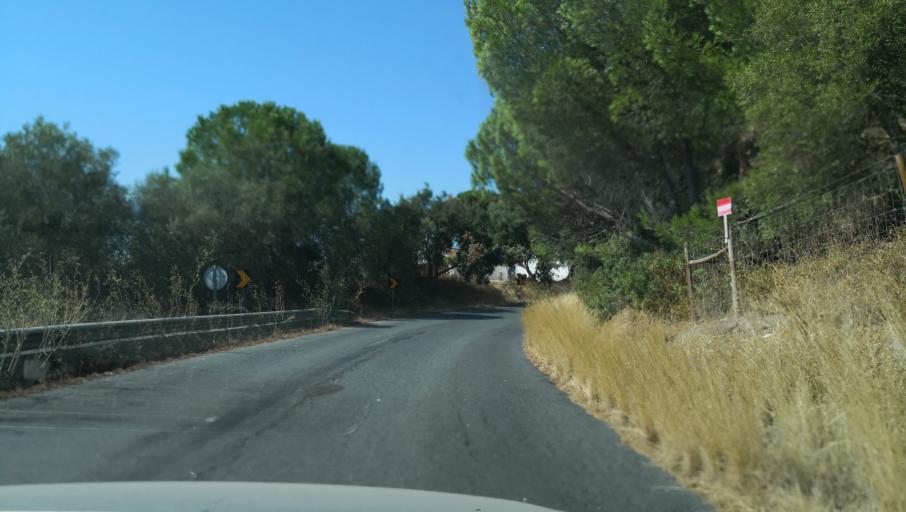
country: PT
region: Setubal
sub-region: Alcacer do Sal
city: Alcacer do Sal
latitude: 38.2783
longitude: -8.3933
